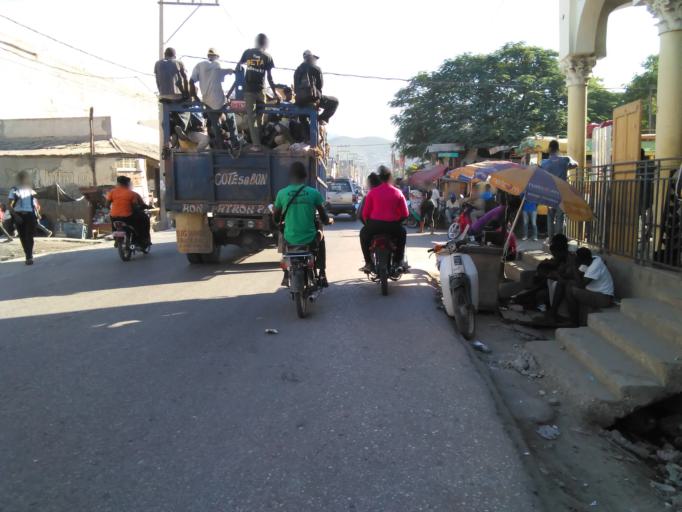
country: HT
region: Artibonite
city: Saint-Marc
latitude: 19.1069
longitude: -72.7011
